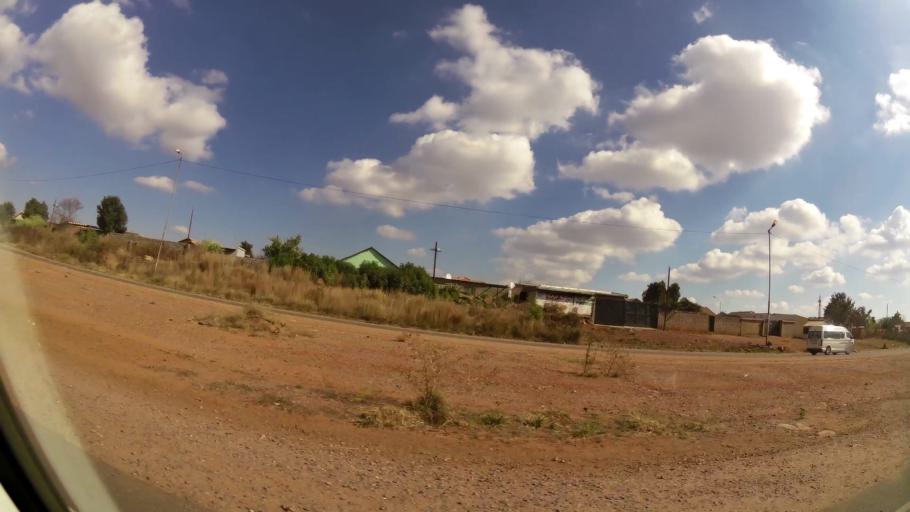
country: ZA
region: Gauteng
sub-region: City of Tshwane Metropolitan Municipality
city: Cullinan
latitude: -25.7022
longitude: 28.4190
